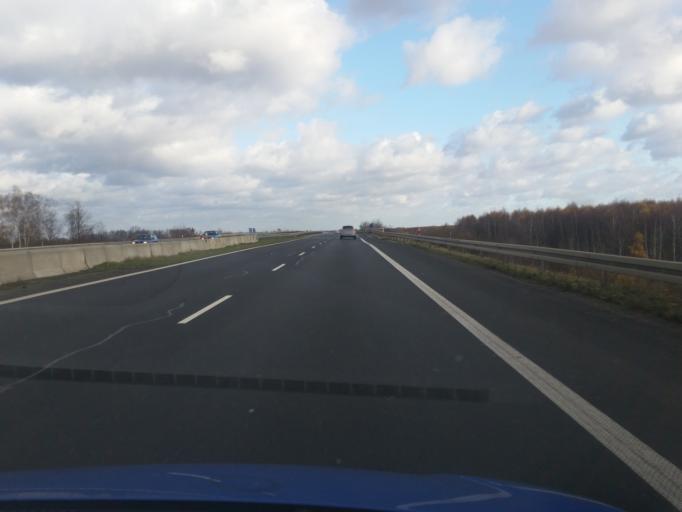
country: PL
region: Silesian Voivodeship
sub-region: Powiat czestochowski
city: Koscielec
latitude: 50.8897
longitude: 19.1785
